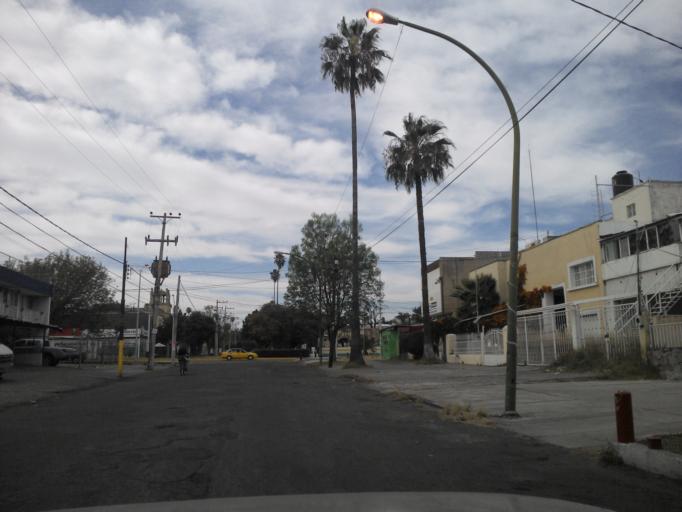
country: MX
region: Jalisco
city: Guadalajara
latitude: 20.6618
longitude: -103.3564
